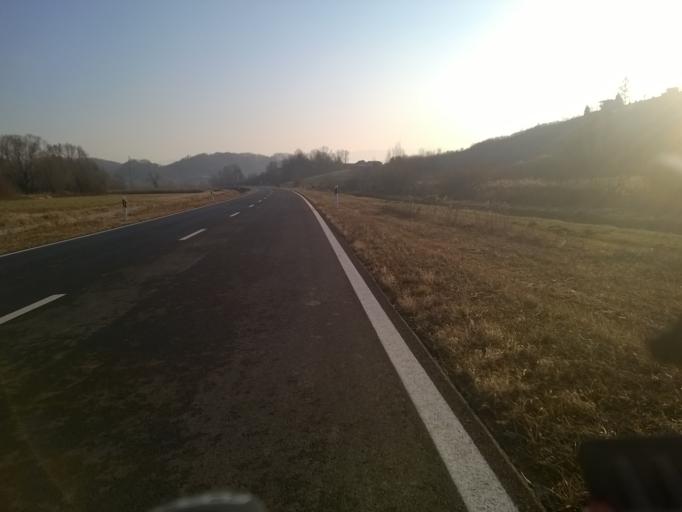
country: HR
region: Krapinsko-Zagorska
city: Zabok
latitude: 46.0414
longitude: 15.9157
